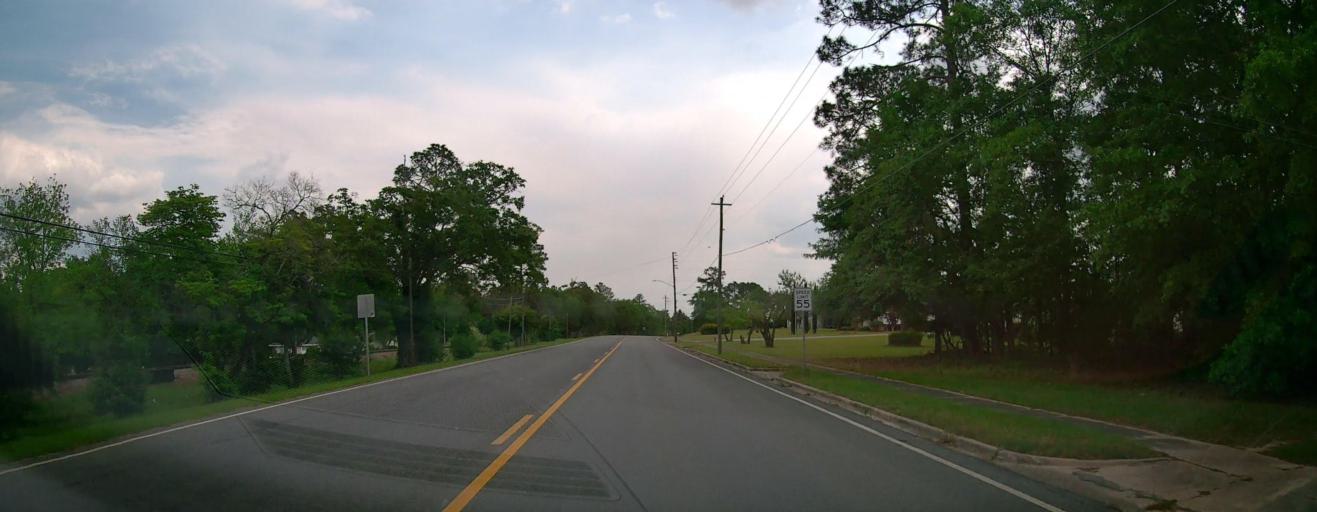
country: US
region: Georgia
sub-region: Treutlen County
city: Soperton
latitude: 32.3691
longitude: -82.5843
